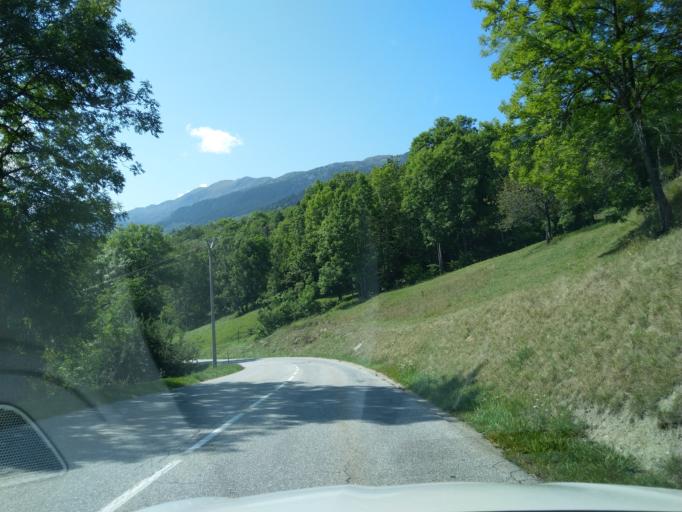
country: FR
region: Rhone-Alpes
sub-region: Departement de la Savoie
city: Les Allues
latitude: 45.4418
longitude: 6.5575
